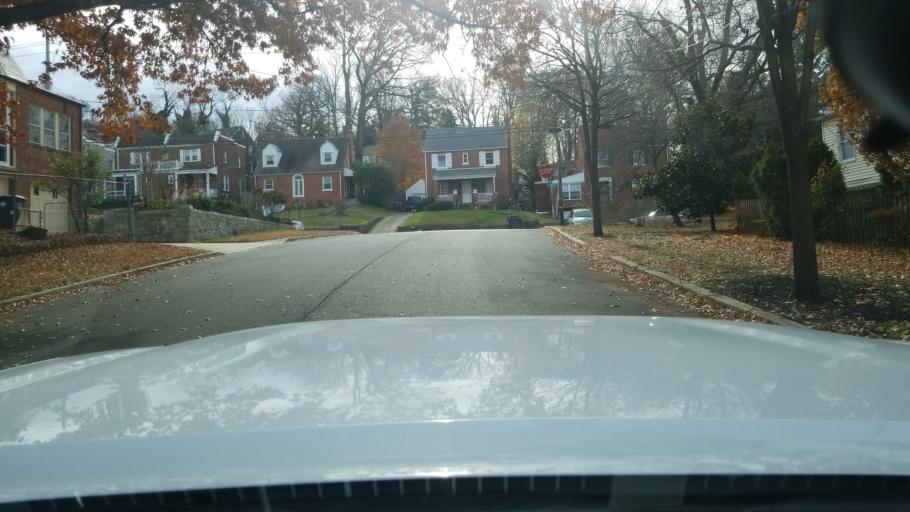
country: US
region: Maryland
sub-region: Prince George's County
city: Silver Hill
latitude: 38.8708
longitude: -76.9567
